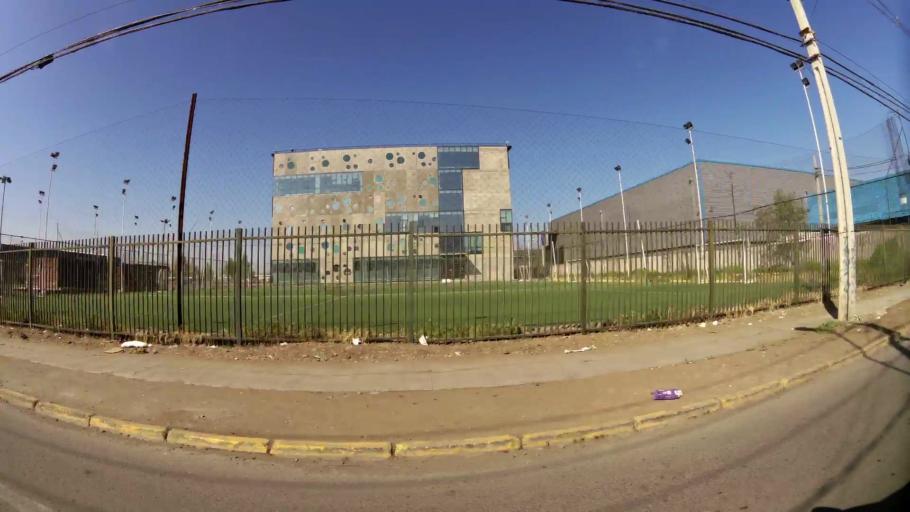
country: CL
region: Santiago Metropolitan
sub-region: Provincia de Chacabuco
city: Chicureo Abajo
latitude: -33.3623
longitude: -70.6781
